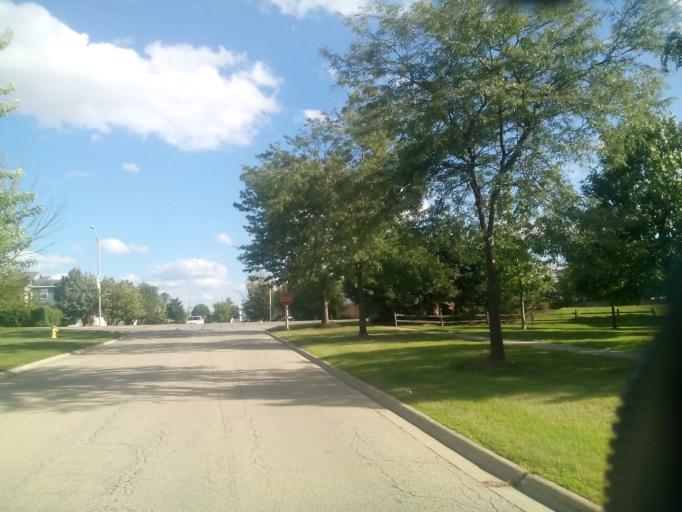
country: US
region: Illinois
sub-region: Will County
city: Plainfield
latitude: 41.6928
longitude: -88.1579
